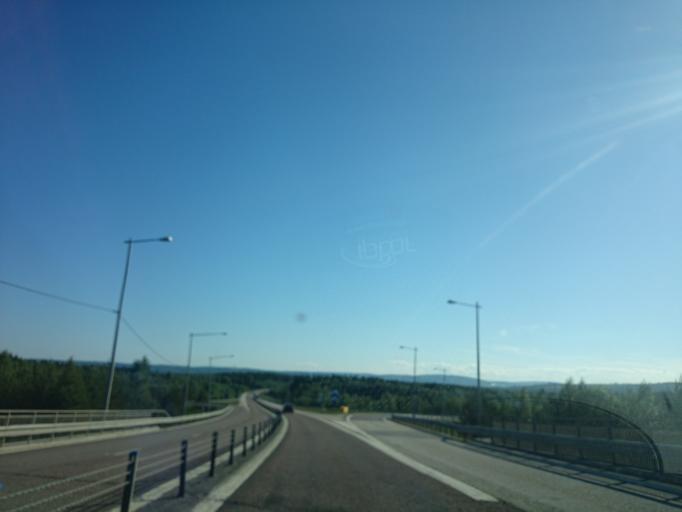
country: SE
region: Vaesternorrland
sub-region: Timra Kommun
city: Soraker
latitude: 62.5267
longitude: 17.4767
